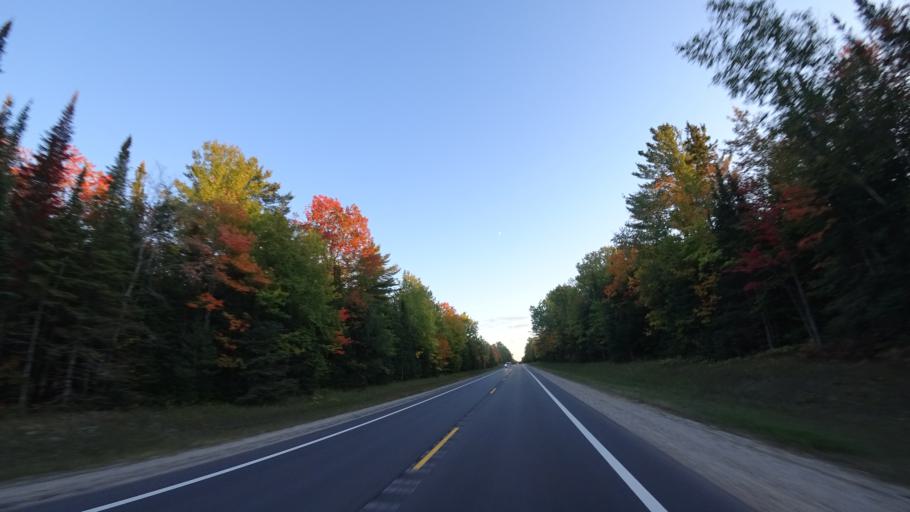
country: US
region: Michigan
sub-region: Mackinac County
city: Saint Ignace
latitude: 46.2710
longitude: -85.0095
